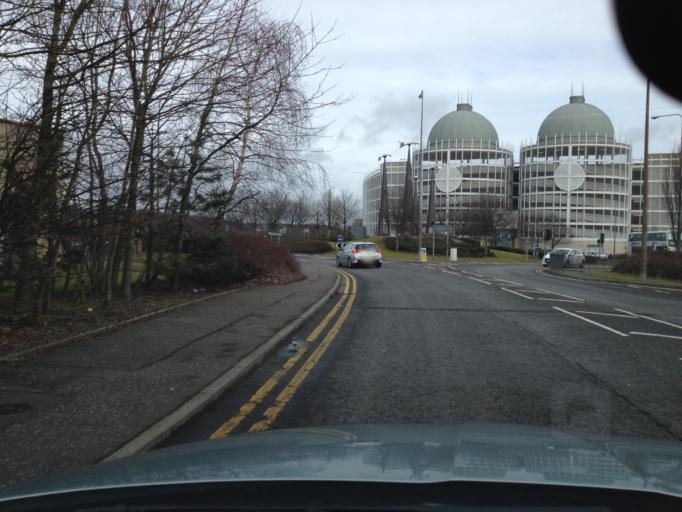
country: GB
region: Scotland
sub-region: West Lothian
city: Livingston
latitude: 55.8816
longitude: -3.5250
